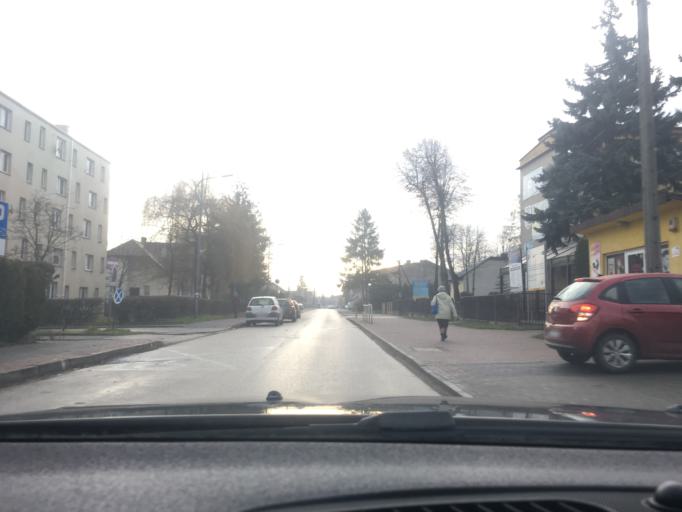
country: PL
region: Swietokrzyskie
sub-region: Powiat jedrzejowski
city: Jedrzejow
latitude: 50.6463
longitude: 20.2918
